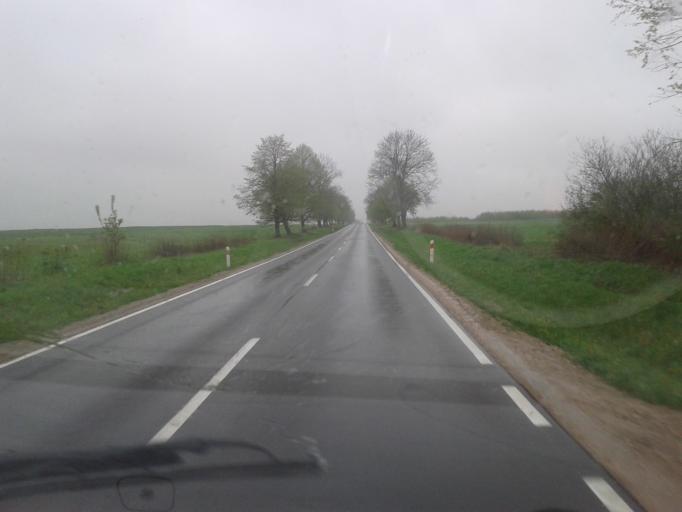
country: PL
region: Subcarpathian Voivodeship
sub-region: Powiat lubaczowski
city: Cieszanow
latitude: 50.2617
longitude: 23.1440
